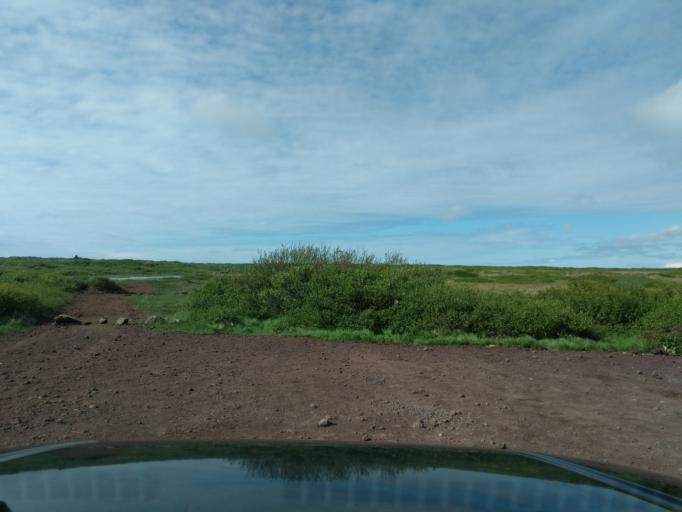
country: IS
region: West
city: Stykkisholmur
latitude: 64.8332
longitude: -22.3164
